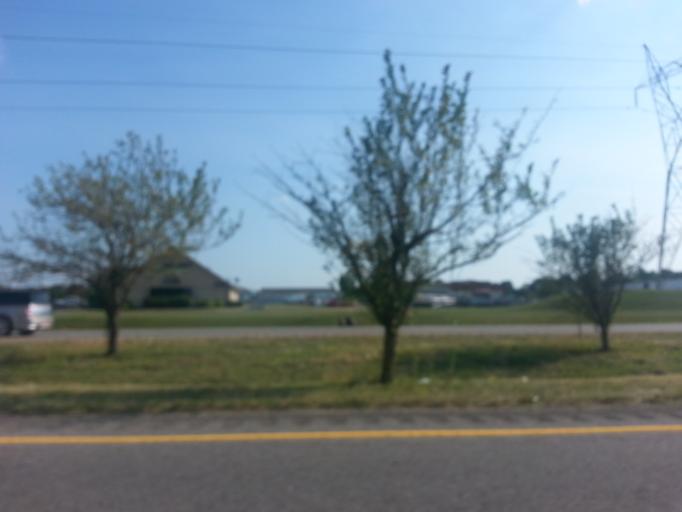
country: US
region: Tennessee
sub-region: Blount County
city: Maryville
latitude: 35.7553
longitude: -84.0205
